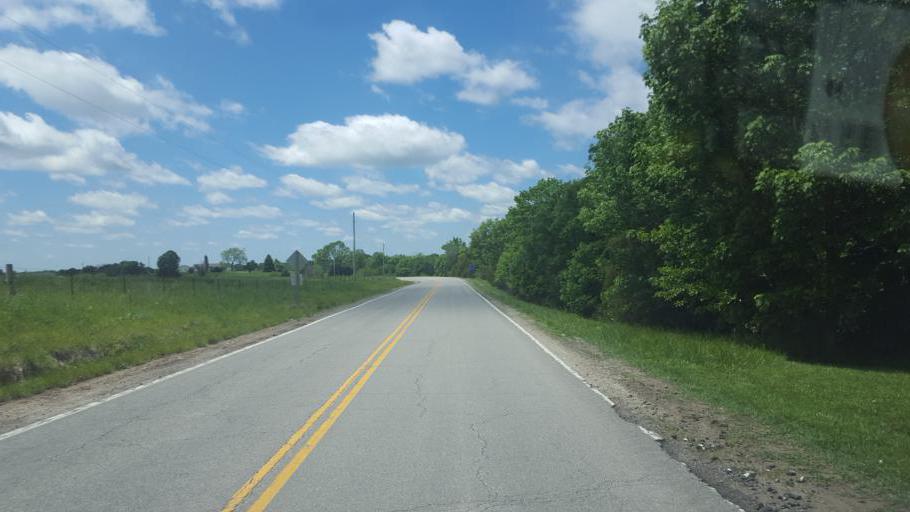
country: US
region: Missouri
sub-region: Harrison County
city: Bethany
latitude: 40.3076
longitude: -94.0242
